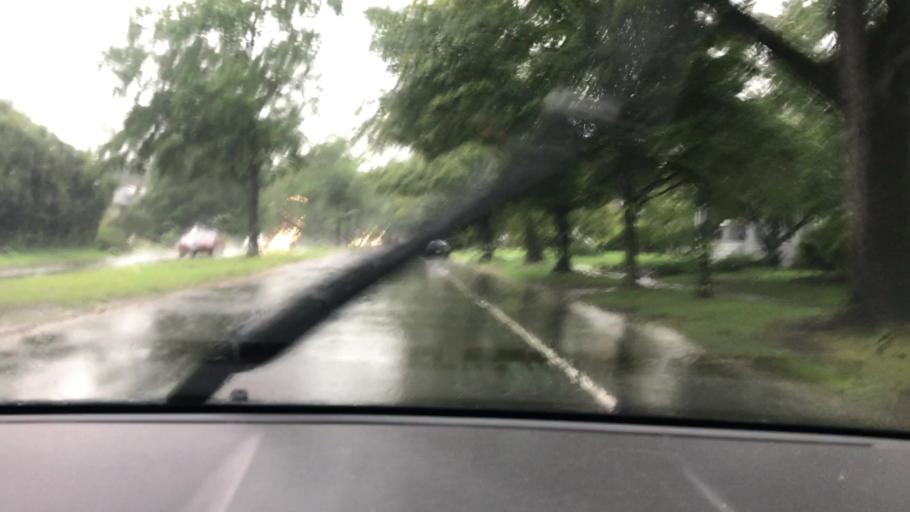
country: US
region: Virginia
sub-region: City of Richmond
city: Richmond
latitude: 37.5844
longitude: -77.4559
